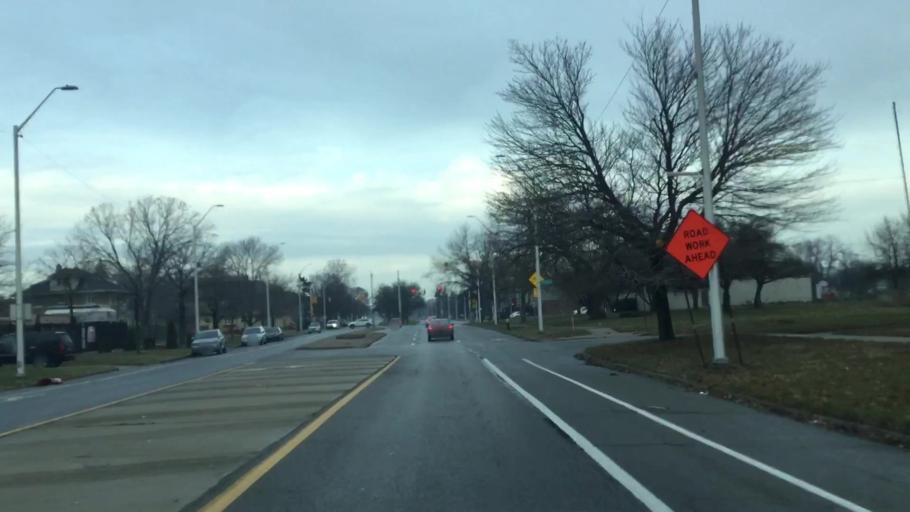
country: US
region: Michigan
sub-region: Wayne County
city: Detroit
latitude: 42.3630
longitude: -83.0122
